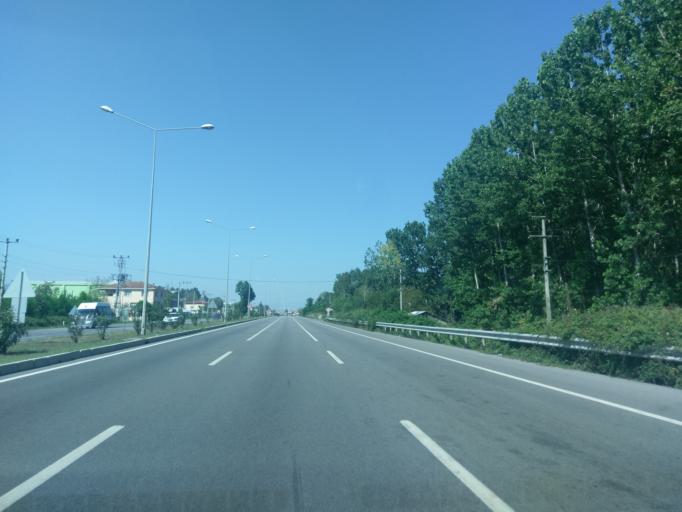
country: TR
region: Samsun
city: Dikbiyik
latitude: 41.2344
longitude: 36.5659
